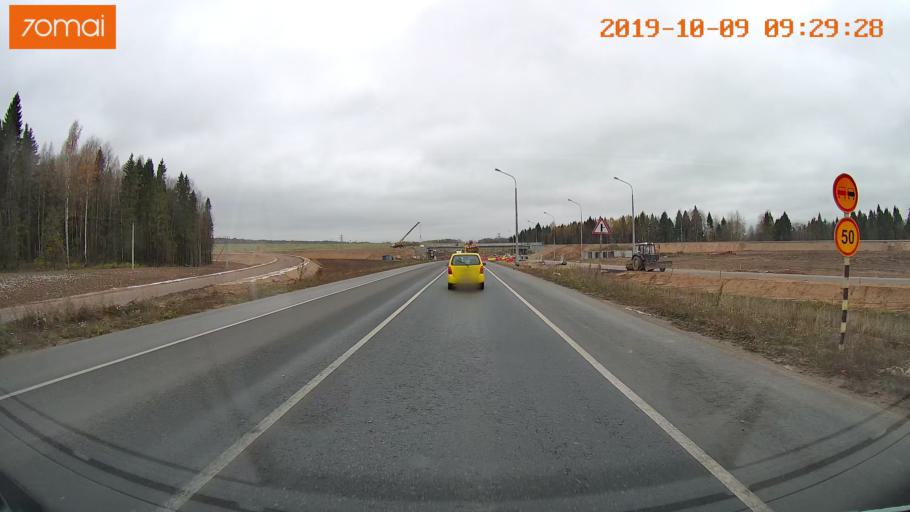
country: RU
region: Vologda
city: Vologda
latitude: 59.1321
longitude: 39.9576
